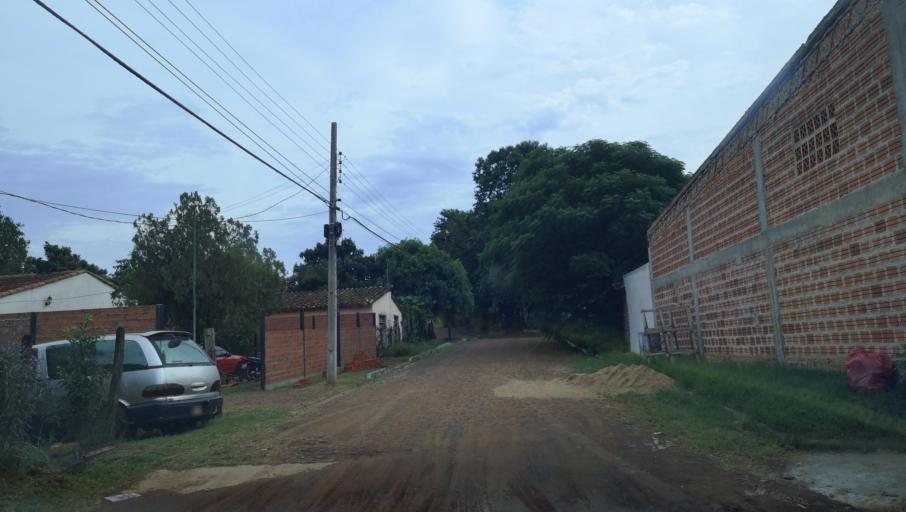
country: PY
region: Misiones
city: Santa Maria
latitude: -26.8826
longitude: -57.0330
